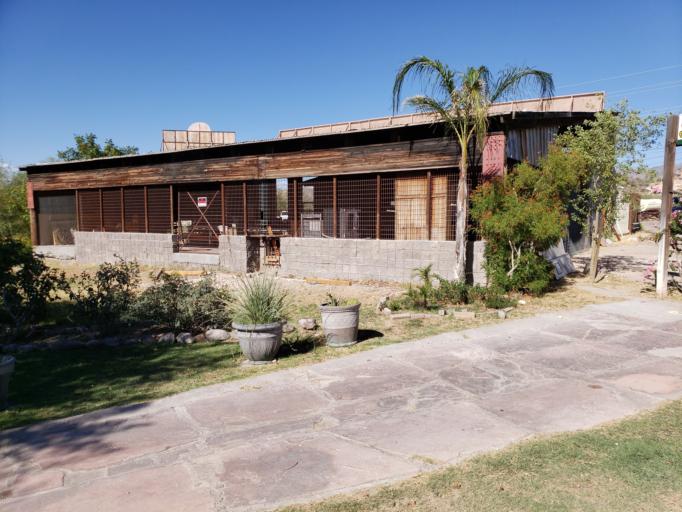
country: US
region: Arizona
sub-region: Yavapai County
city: Black Canyon City
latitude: 34.0488
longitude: -112.1493
